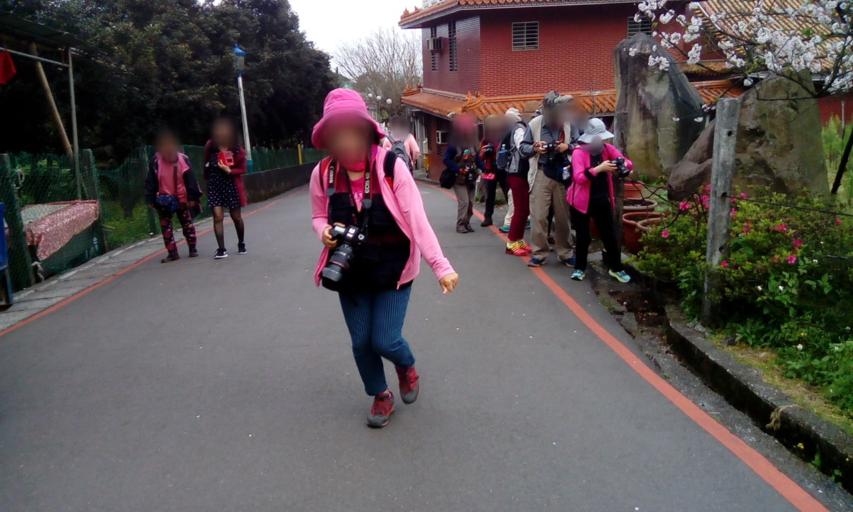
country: TW
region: Taipei
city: Taipei
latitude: 25.1860
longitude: 121.4850
